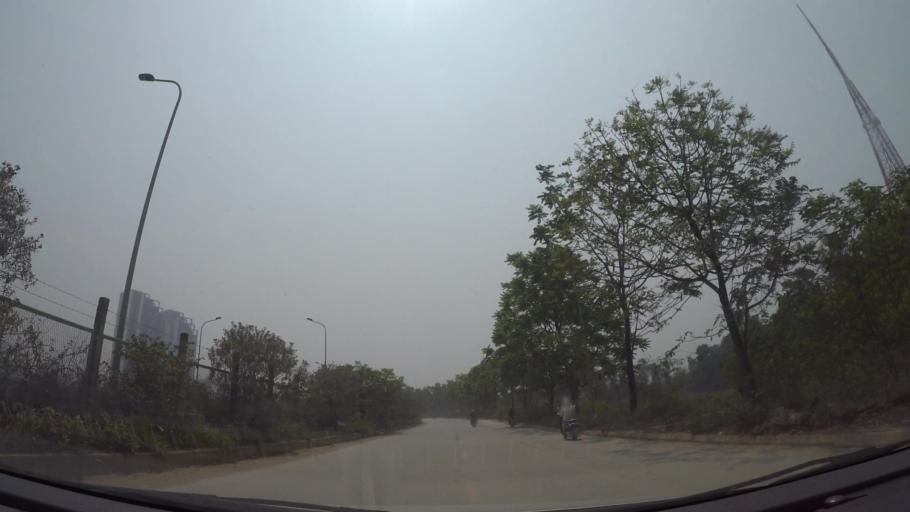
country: VN
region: Ha Noi
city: Cau Dien
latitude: 21.0051
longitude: 105.7640
